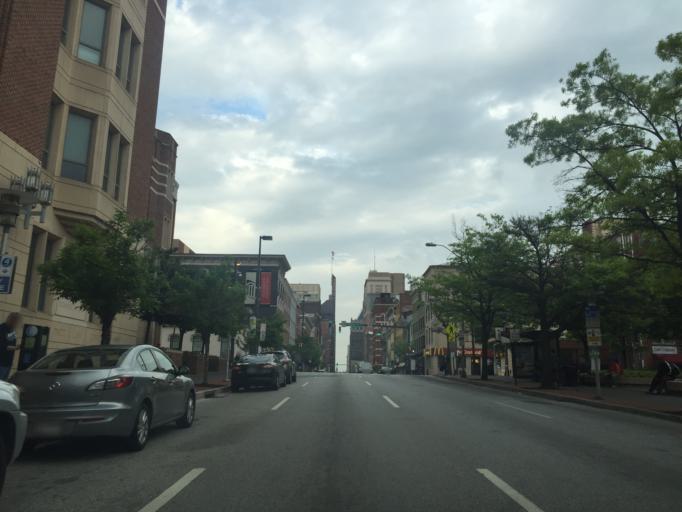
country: US
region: Maryland
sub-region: City of Baltimore
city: Baltimore
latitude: 39.2893
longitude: -76.6231
